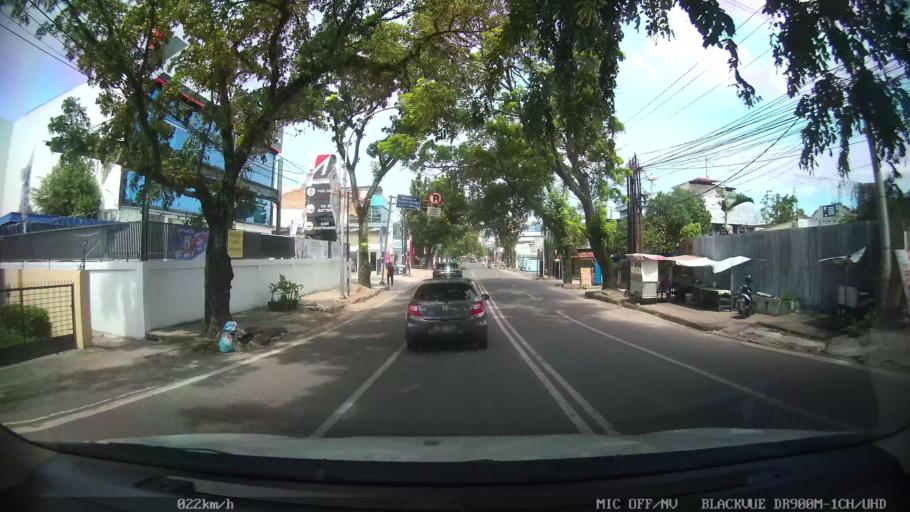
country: ID
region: North Sumatra
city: Medan
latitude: 3.5847
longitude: 98.6558
